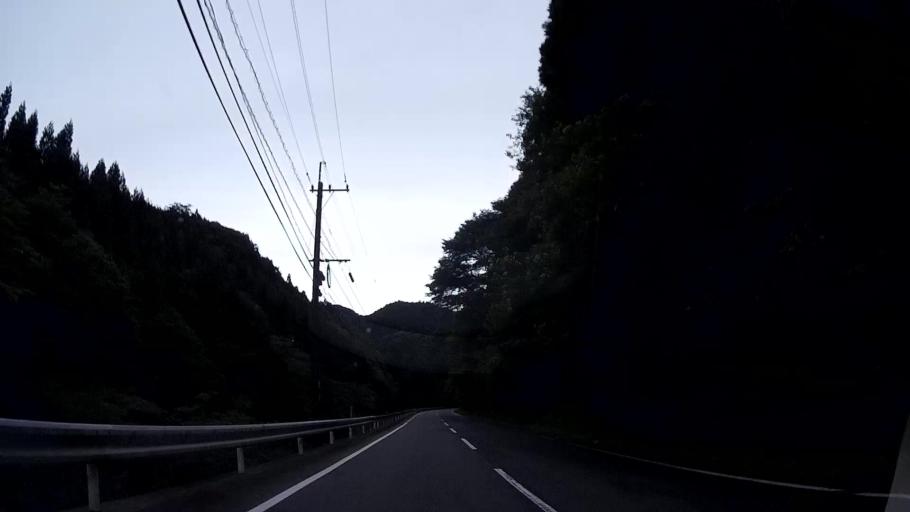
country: JP
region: Kumamoto
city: Kikuchi
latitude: 33.0726
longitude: 130.9190
